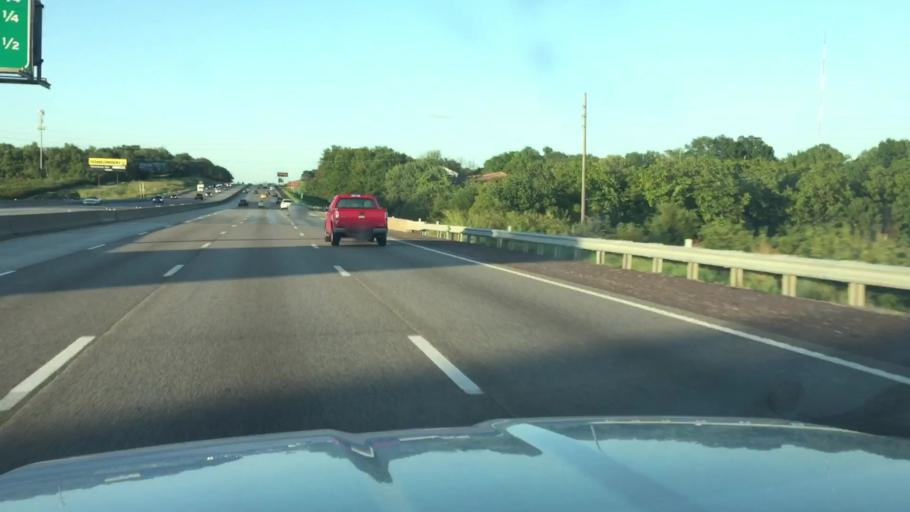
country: US
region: Missouri
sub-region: Saint Louis County
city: Saint George
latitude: 38.5240
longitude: -90.3203
